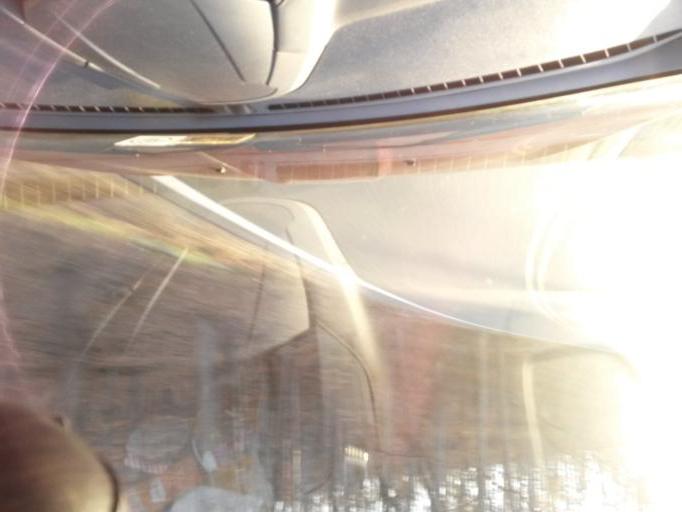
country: US
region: Virginia
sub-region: City of Buena Vista
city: Buena Vista
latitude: 37.7506
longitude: -79.2781
